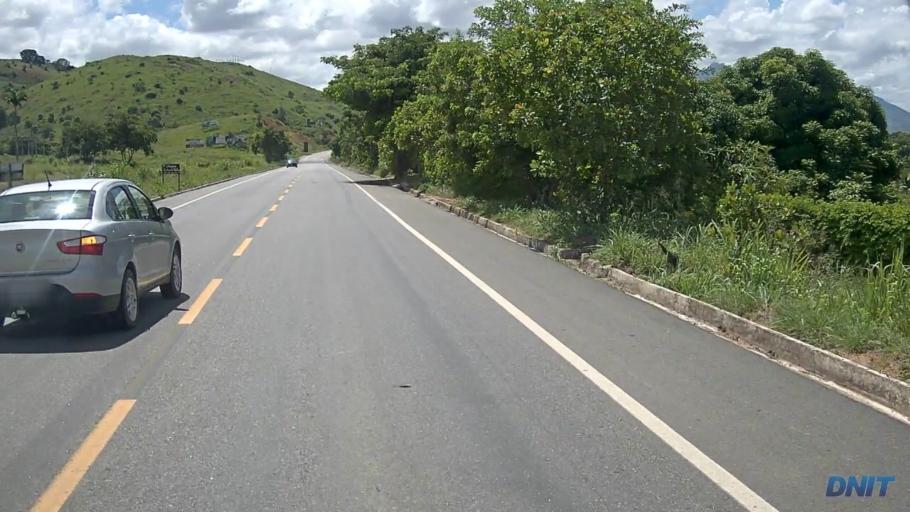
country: BR
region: Minas Gerais
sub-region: Governador Valadares
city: Governador Valadares
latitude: -18.9337
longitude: -42.0513
